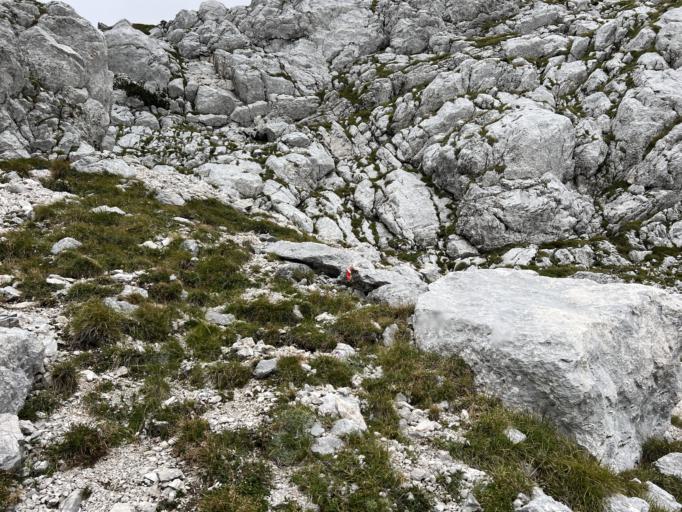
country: IT
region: Friuli Venezia Giulia
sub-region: Provincia di Udine
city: Resiutta
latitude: 46.3497
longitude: 13.2243
